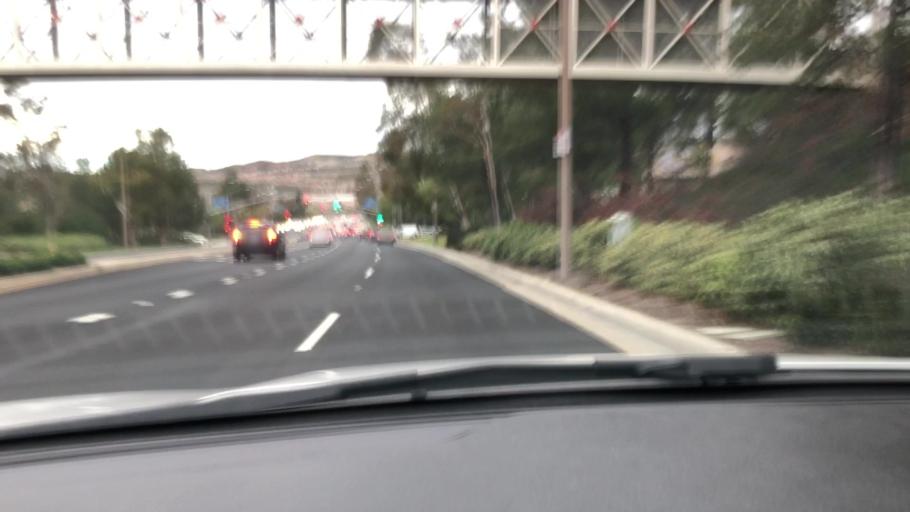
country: US
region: California
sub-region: Los Angeles County
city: Valencia
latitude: 34.4623
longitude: -118.5465
